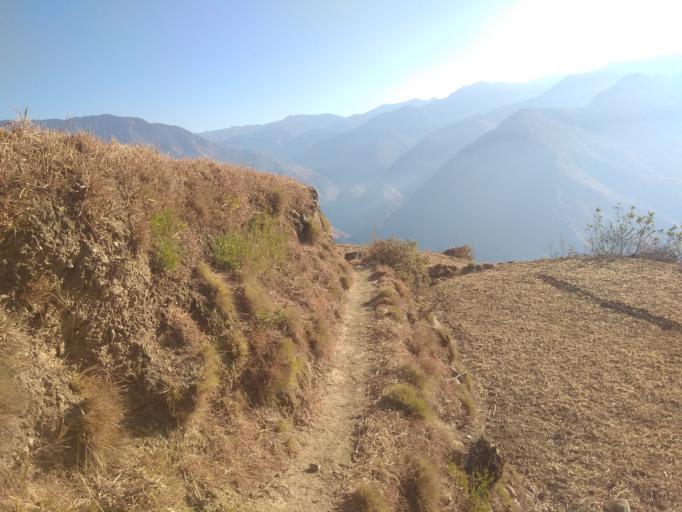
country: NP
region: Mid Western
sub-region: Karnali Zone
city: Jumla
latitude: 29.3138
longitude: 81.7339
